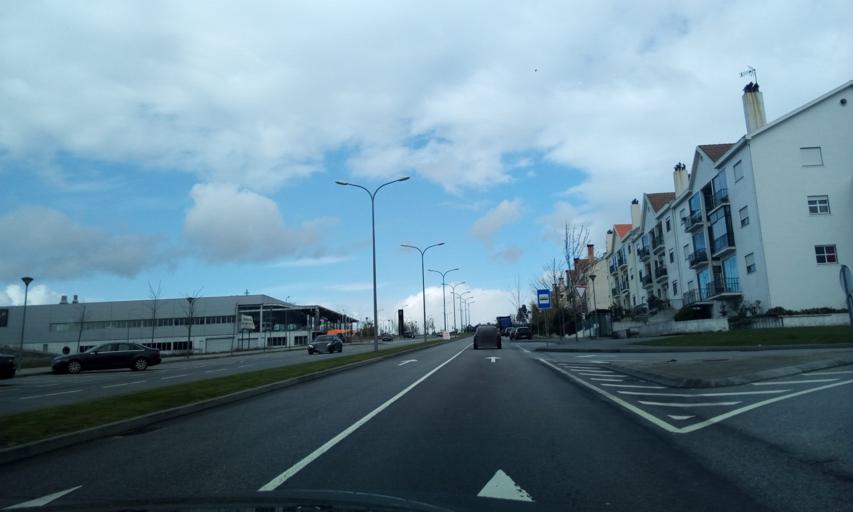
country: PT
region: Viseu
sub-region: Viseu
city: Viseu
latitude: 40.6319
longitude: -7.9092
